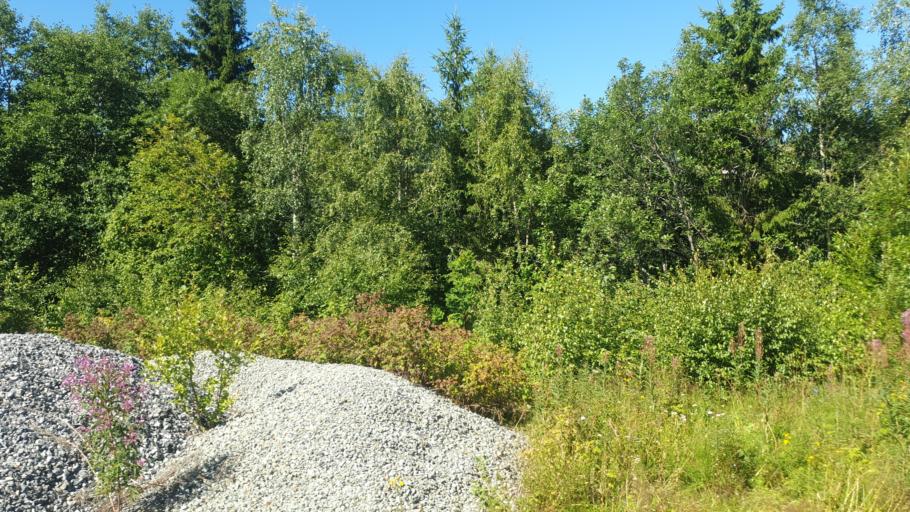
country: NO
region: Sor-Trondelag
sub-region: Meldal
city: Meldal
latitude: 63.1695
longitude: 9.7483
